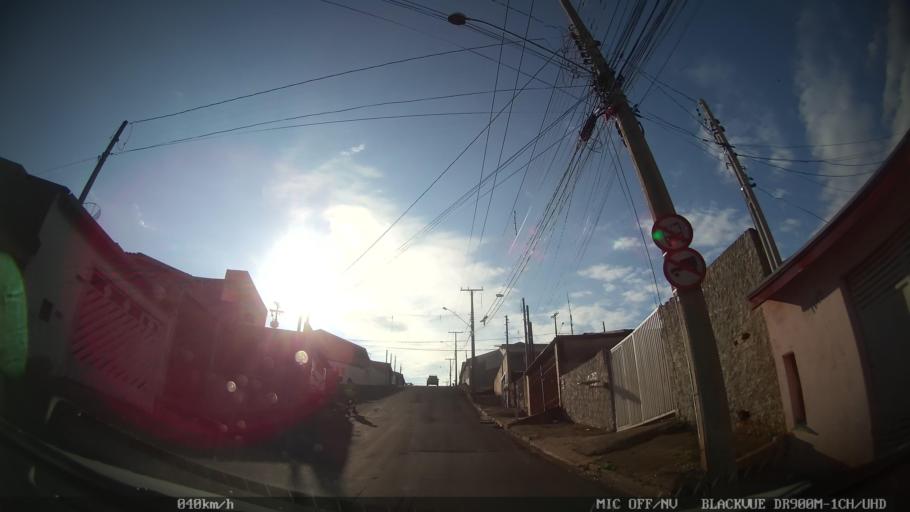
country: BR
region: Sao Paulo
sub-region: Americana
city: Americana
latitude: -22.7259
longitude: -47.3738
